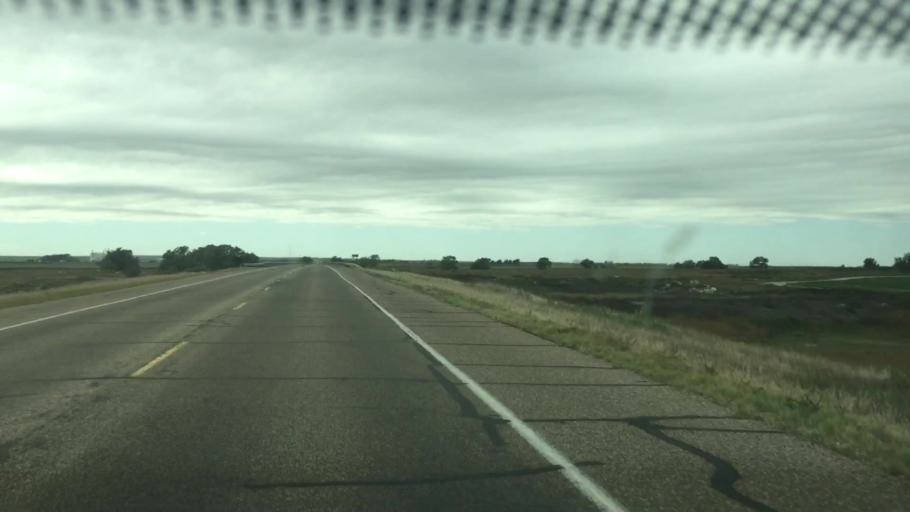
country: US
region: Colorado
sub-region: Prowers County
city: Lamar
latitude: 38.0574
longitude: -102.2255
